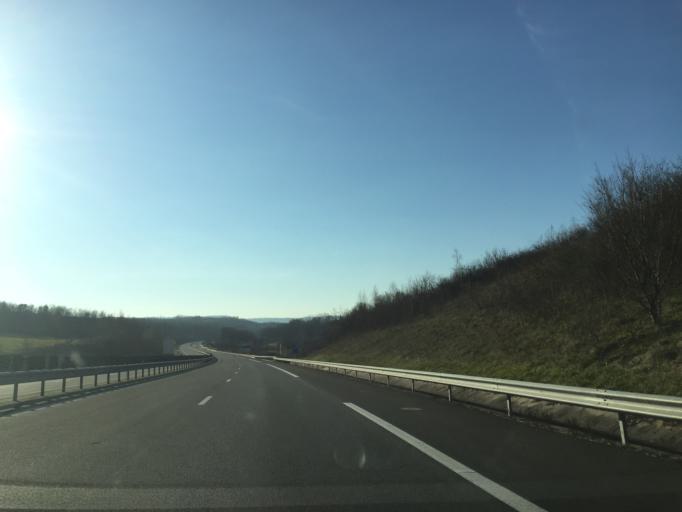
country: FR
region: Limousin
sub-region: Departement de la Correze
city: Mansac
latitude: 45.1621
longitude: 1.3999
